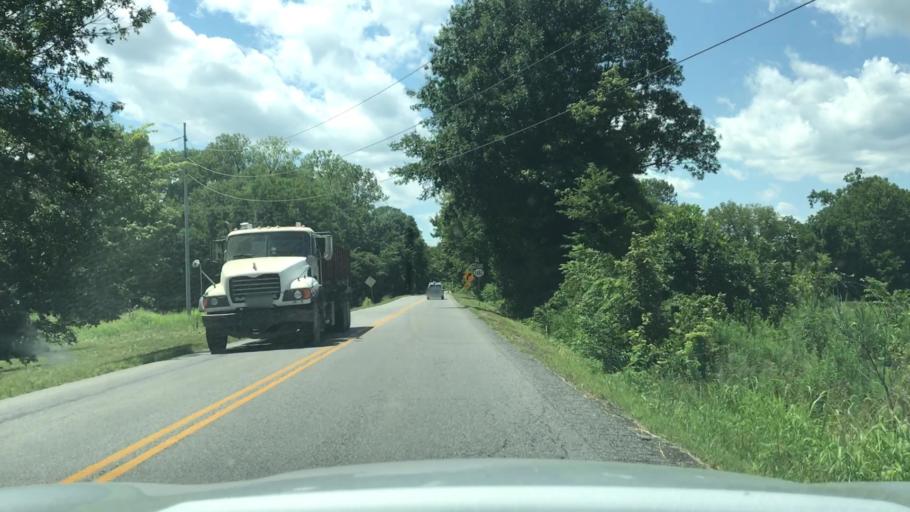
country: US
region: Kentucky
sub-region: Christian County
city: Hopkinsville
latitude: 36.8892
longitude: -87.4554
